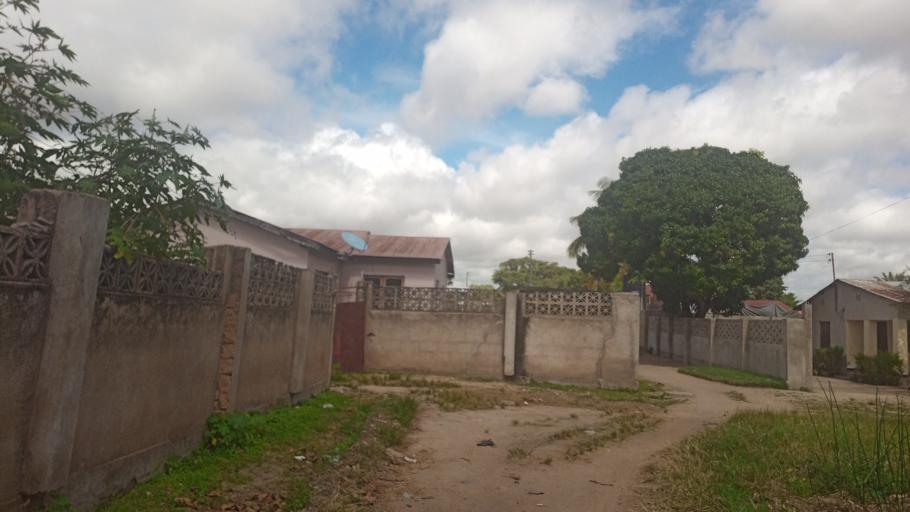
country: TZ
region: Dodoma
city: Dodoma
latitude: -6.1915
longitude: 35.7335
